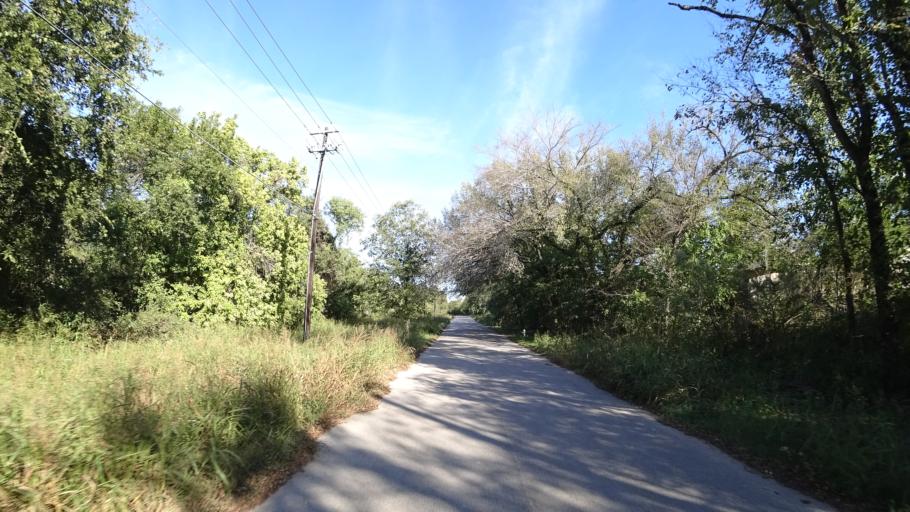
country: US
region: Texas
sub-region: Travis County
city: Austin
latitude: 30.2622
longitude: -97.6712
